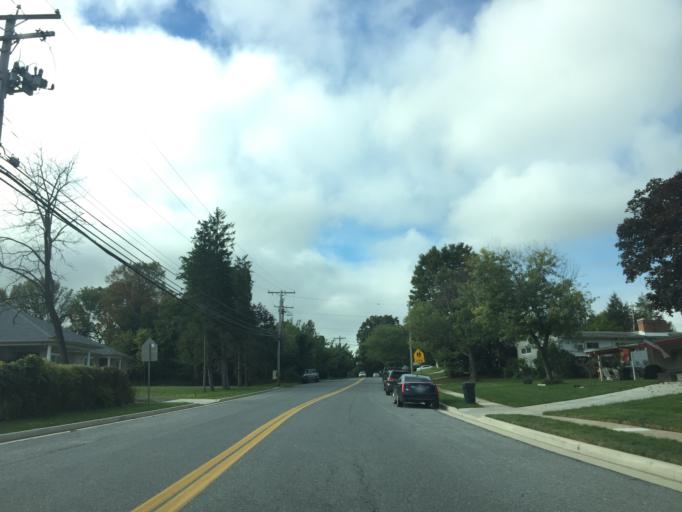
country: US
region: Maryland
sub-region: Baltimore County
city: Pikesville
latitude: 39.3789
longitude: -76.6755
